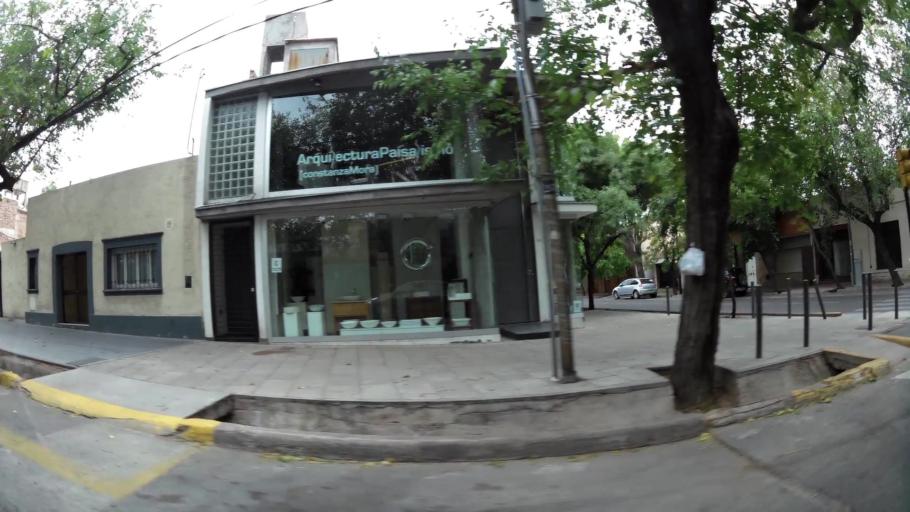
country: AR
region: Mendoza
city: Mendoza
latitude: -32.8938
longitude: -68.8373
